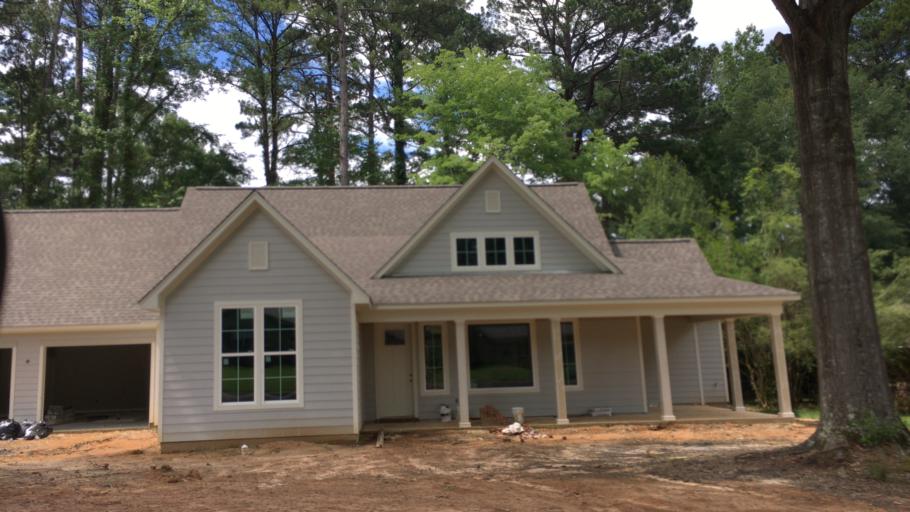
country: US
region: Louisiana
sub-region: Lincoln Parish
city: Ruston
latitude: 32.5480
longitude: -92.6371
